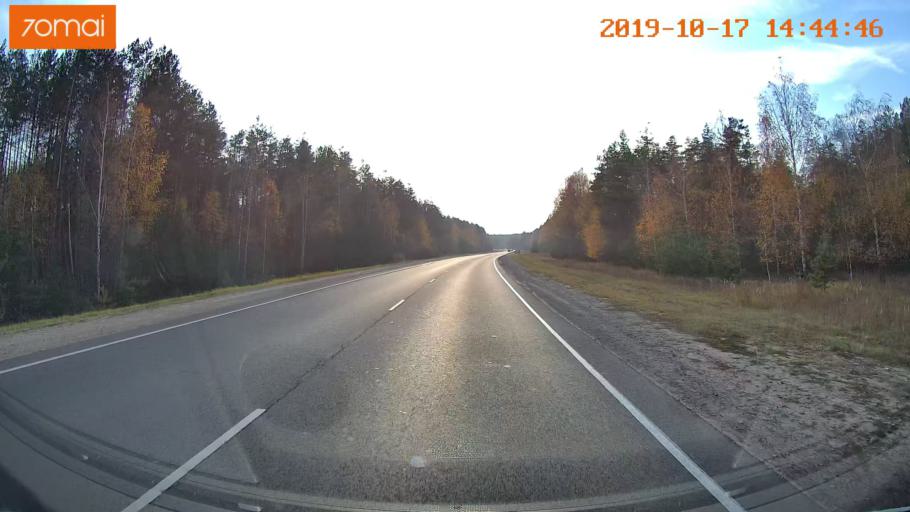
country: RU
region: Rjazan
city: Solotcha
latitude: 54.8082
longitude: 39.8873
